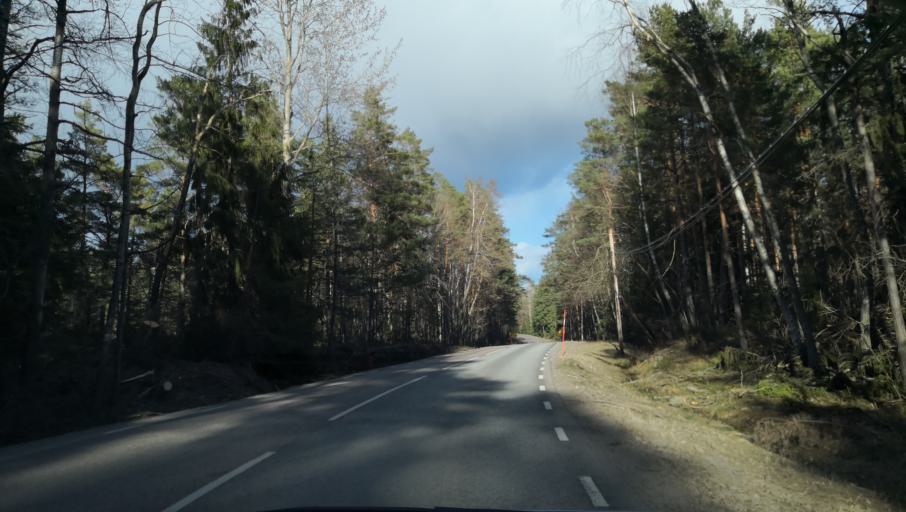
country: SE
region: Stockholm
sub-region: Varmdo Kommun
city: Hemmesta
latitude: 59.2790
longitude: 18.4767
